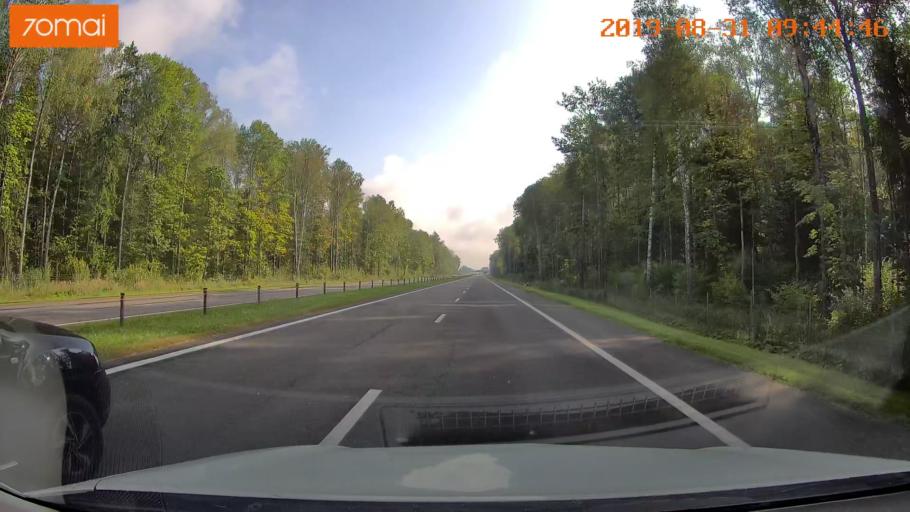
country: BY
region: Mogilev
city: Byalynichy
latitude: 53.9369
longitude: 29.5541
